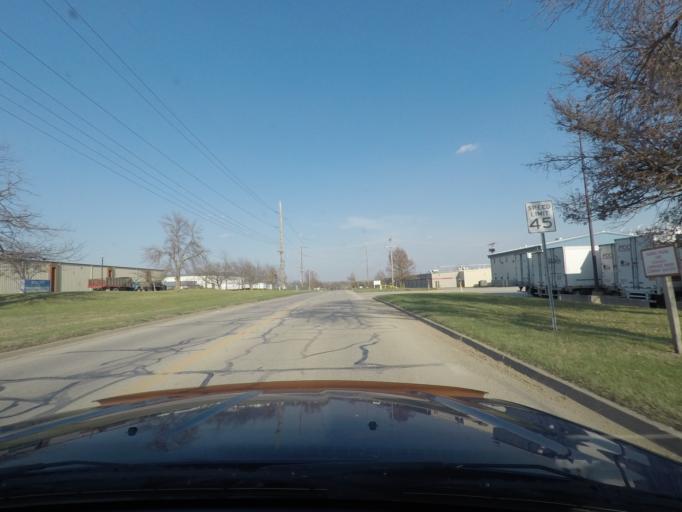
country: US
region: Kansas
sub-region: Douglas County
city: Lawrence
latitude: 39.0006
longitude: -95.2671
